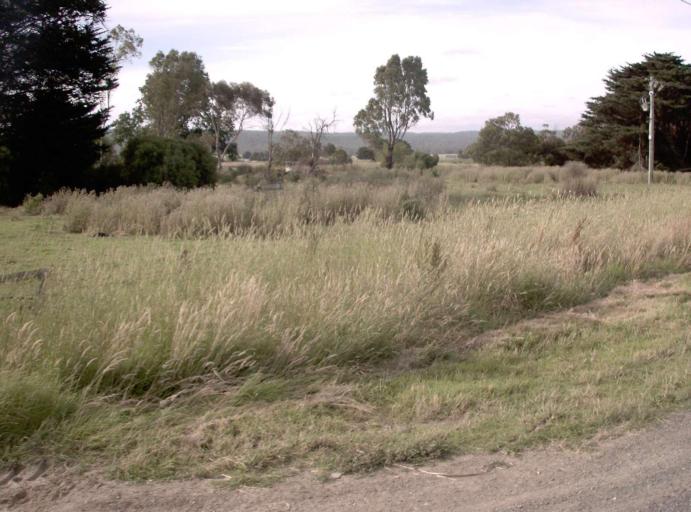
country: AU
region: Victoria
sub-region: Latrobe
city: Traralgon
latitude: -38.0983
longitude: 146.5959
